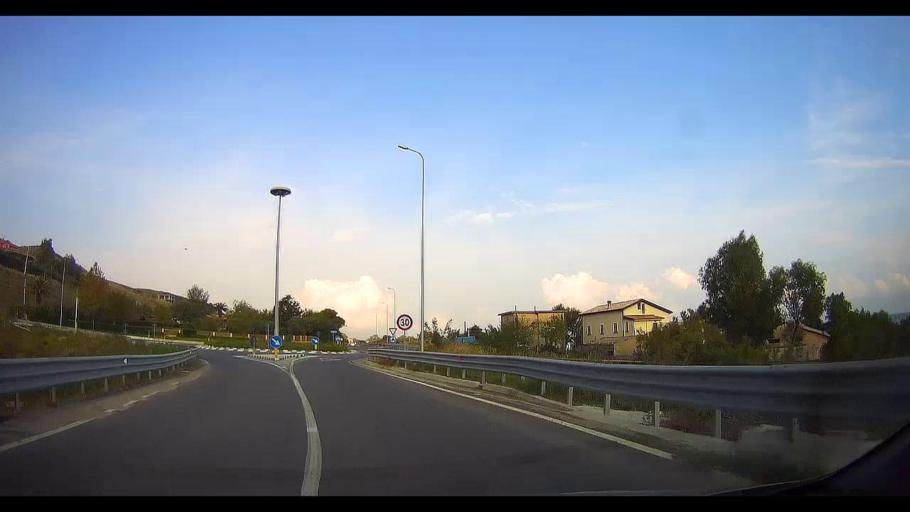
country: IT
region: Calabria
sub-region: Provincia di Cosenza
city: Cariati
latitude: 39.5171
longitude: 16.9108
